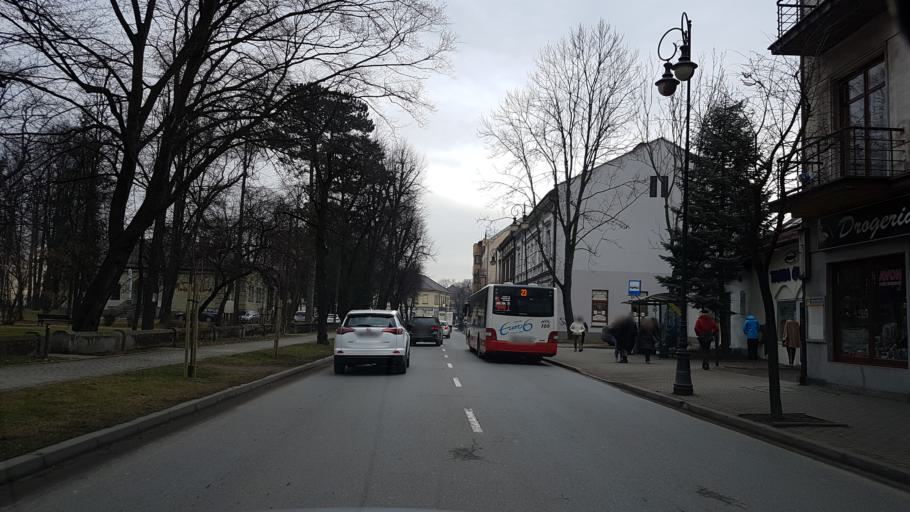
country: PL
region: Lesser Poland Voivodeship
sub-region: Powiat nowosadecki
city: Nowy Sacz
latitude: 49.6200
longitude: 20.6937
